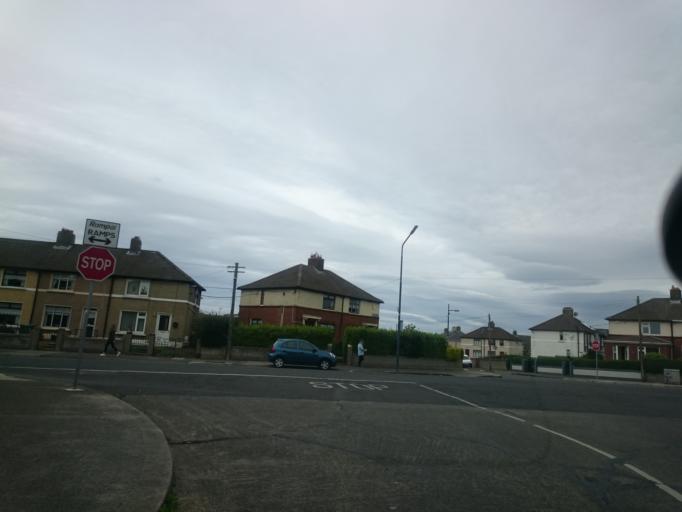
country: IE
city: Greenhills
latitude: 53.3261
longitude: -6.3035
